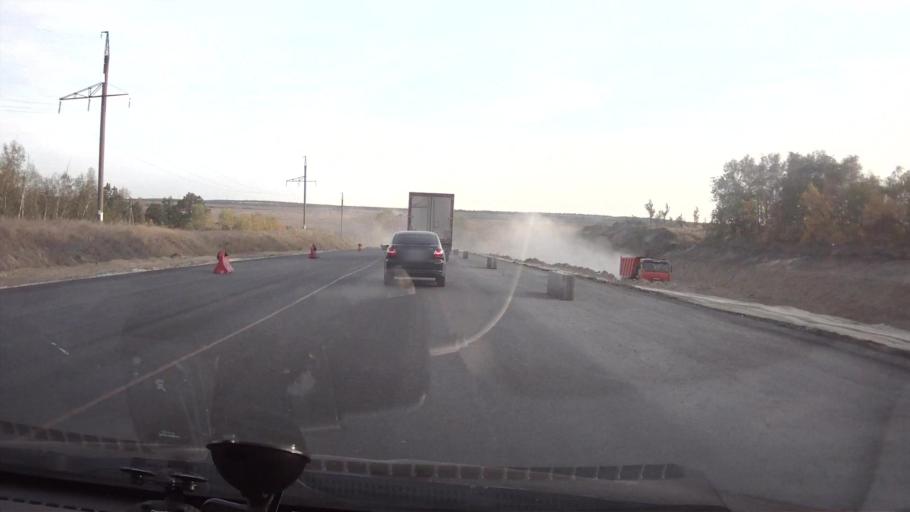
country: RU
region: Saratov
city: Krasnoarmeysk
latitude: 51.2299
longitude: 45.6468
